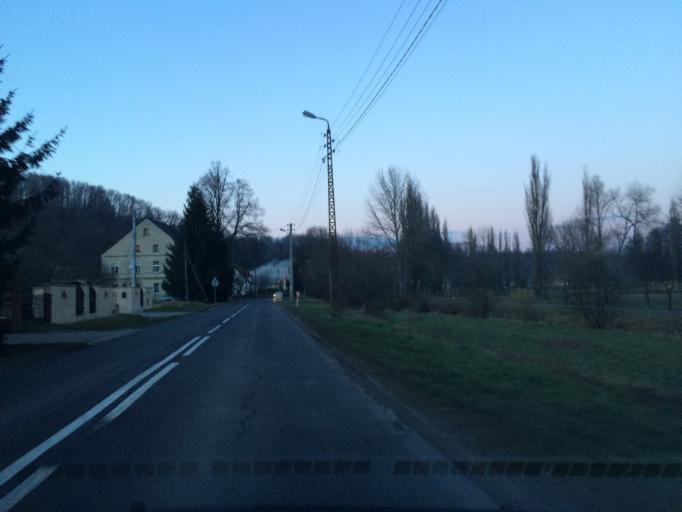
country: PL
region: Lower Silesian Voivodeship
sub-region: Powiat zlotoryjski
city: Zlotoryja
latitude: 51.1243
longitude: 15.8988
